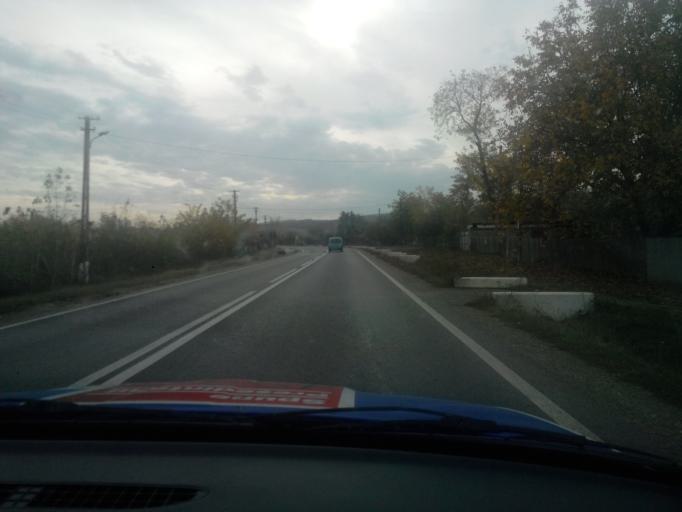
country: RO
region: Vaslui
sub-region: Comuna Pogonesti
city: Pogonesti
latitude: 46.1608
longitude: 27.5905
